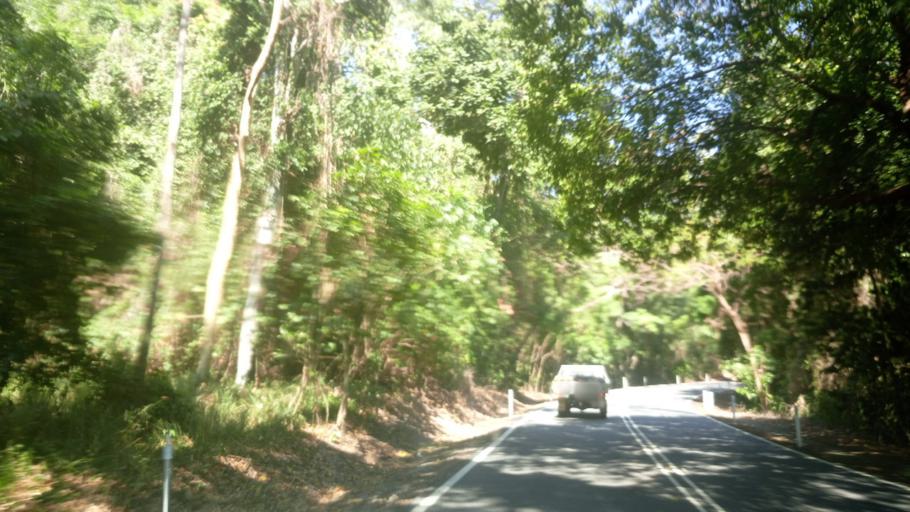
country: AU
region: Queensland
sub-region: Cairns
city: Palm Cove
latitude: -16.7356
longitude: 145.6608
